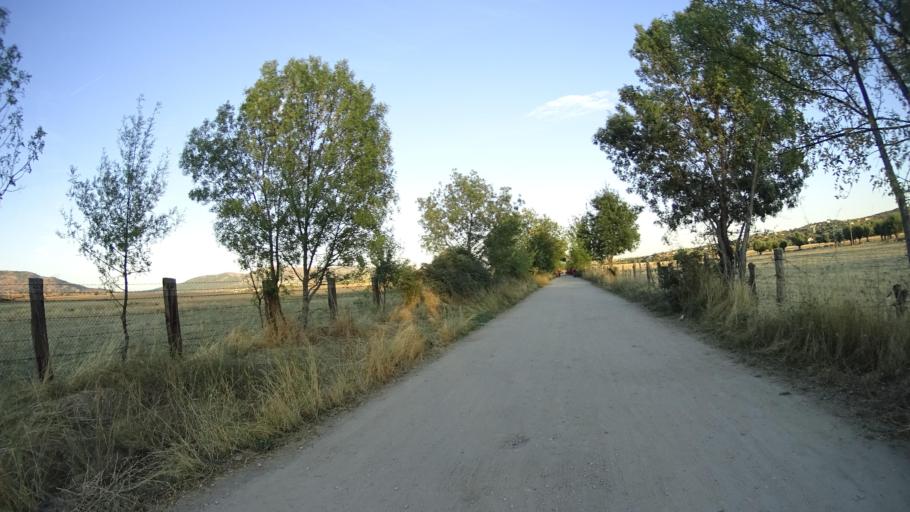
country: ES
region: Madrid
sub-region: Provincia de Madrid
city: Navalquejigo
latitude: 40.6377
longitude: -4.0479
